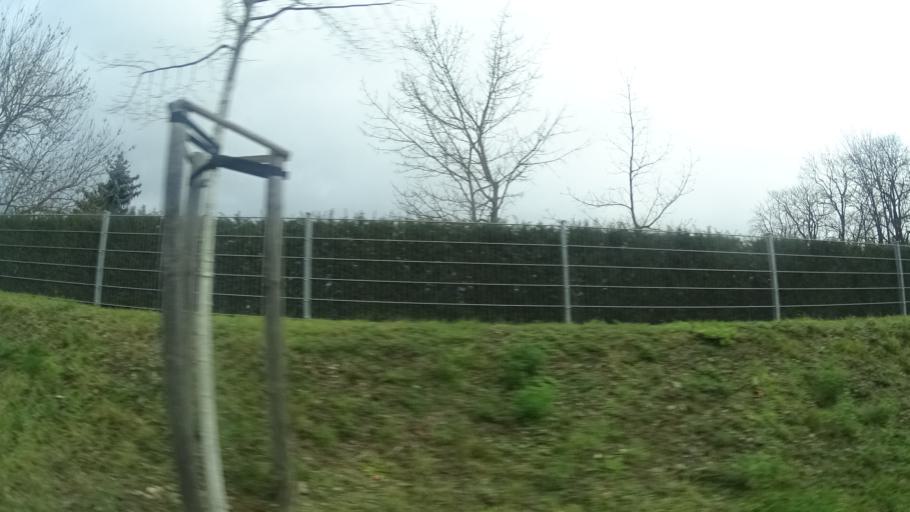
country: DE
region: Thuringia
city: Saalfeld
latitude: 50.6506
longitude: 11.3436
